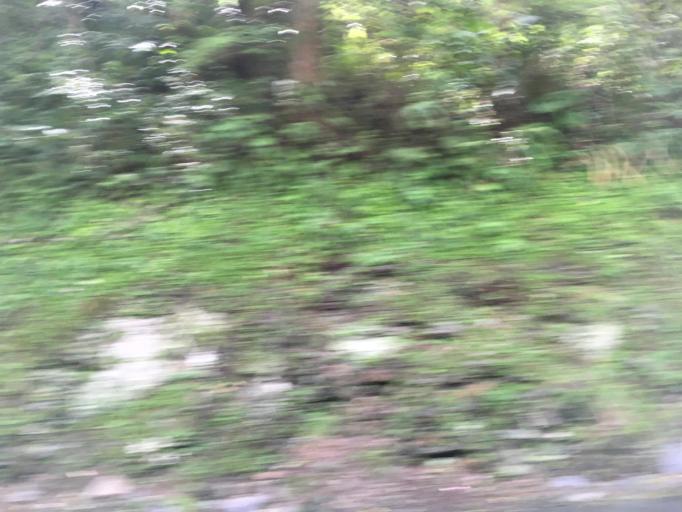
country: TW
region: Taiwan
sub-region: Yilan
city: Yilan
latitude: 24.5787
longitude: 121.4831
